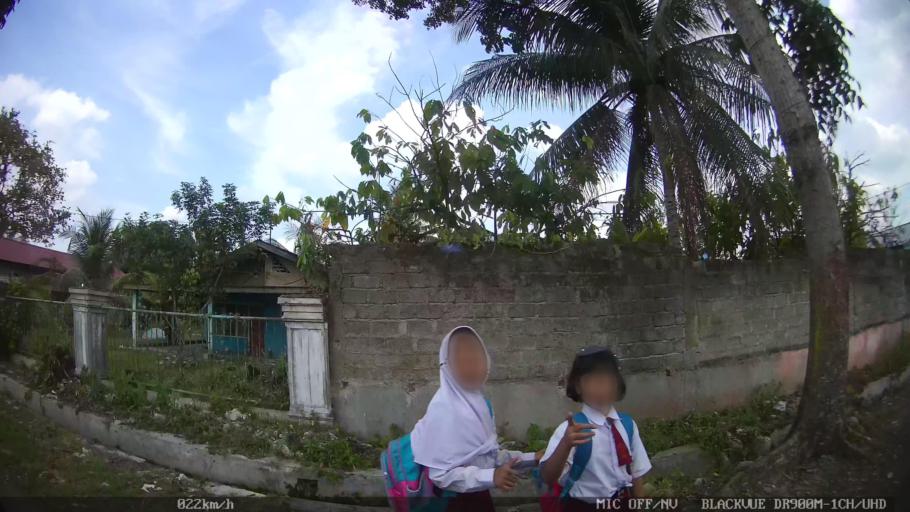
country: ID
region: North Sumatra
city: Binjai
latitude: 3.6281
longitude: 98.5171
